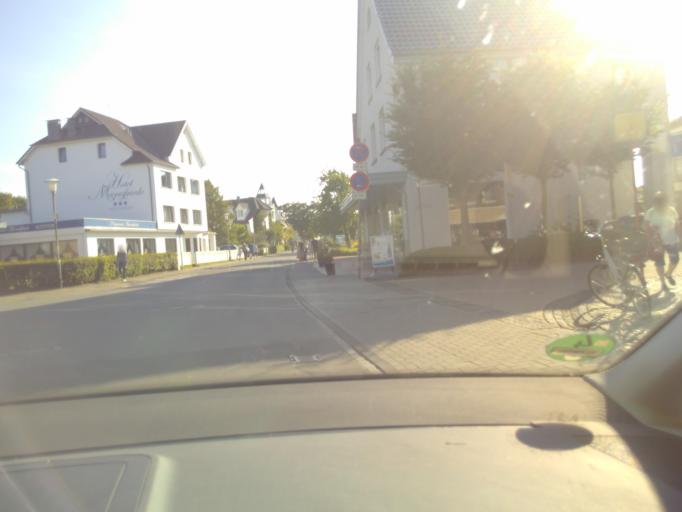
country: DE
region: Lower Saxony
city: Cuxhaven
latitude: 53.8845
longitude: 8.6404
